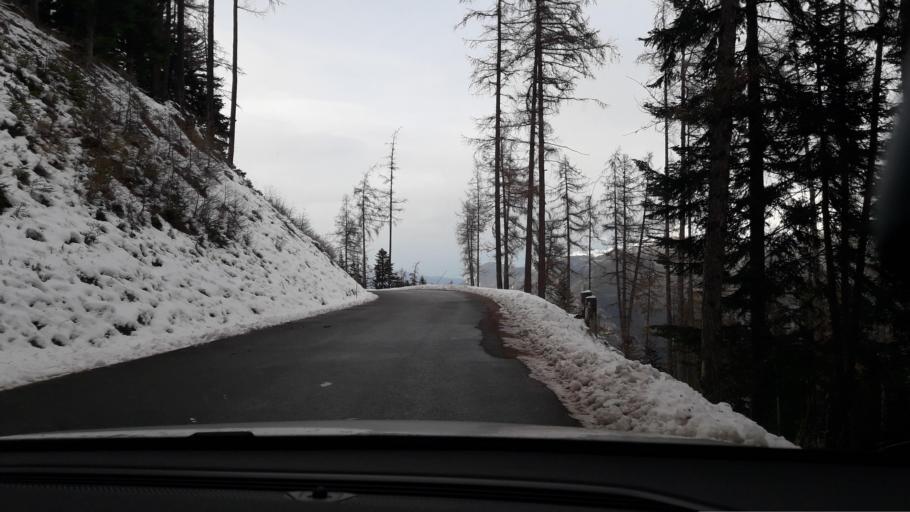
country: FR
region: Rhone-Alpes
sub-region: Departement de la Savoie
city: Saint-Michel-de-Maurienne
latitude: 45.2229
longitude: 6.4148
